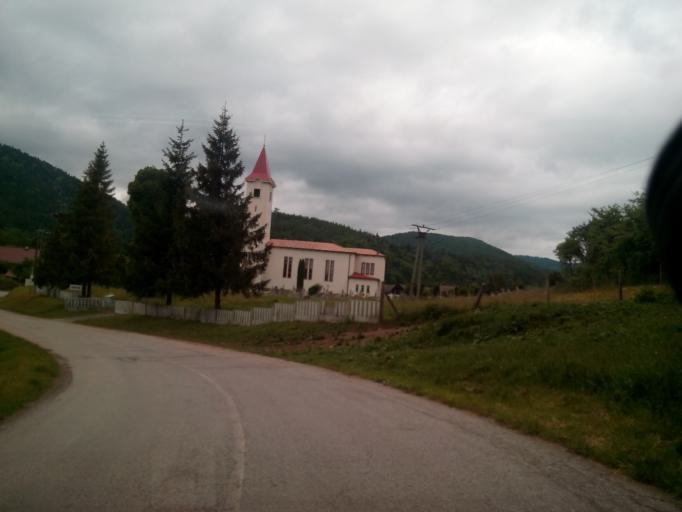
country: SK
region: Presovsky
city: Lipany
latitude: 49.0353
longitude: 20.9466
